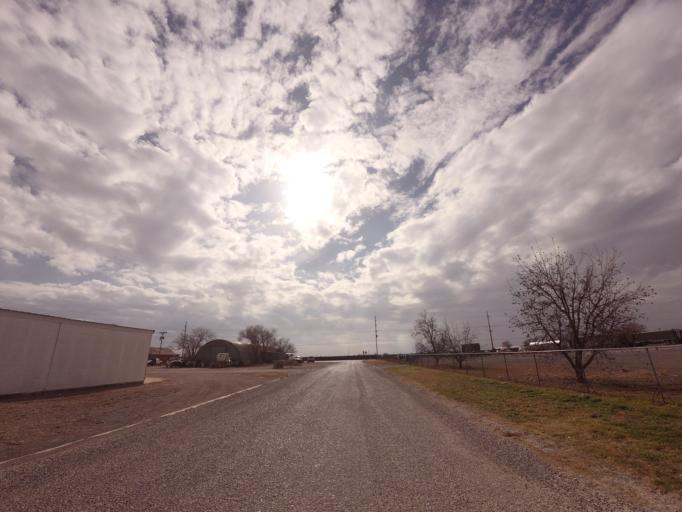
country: US
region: New Mexico
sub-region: Curry County
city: Clovis
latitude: 34.3912
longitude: -103.2180
